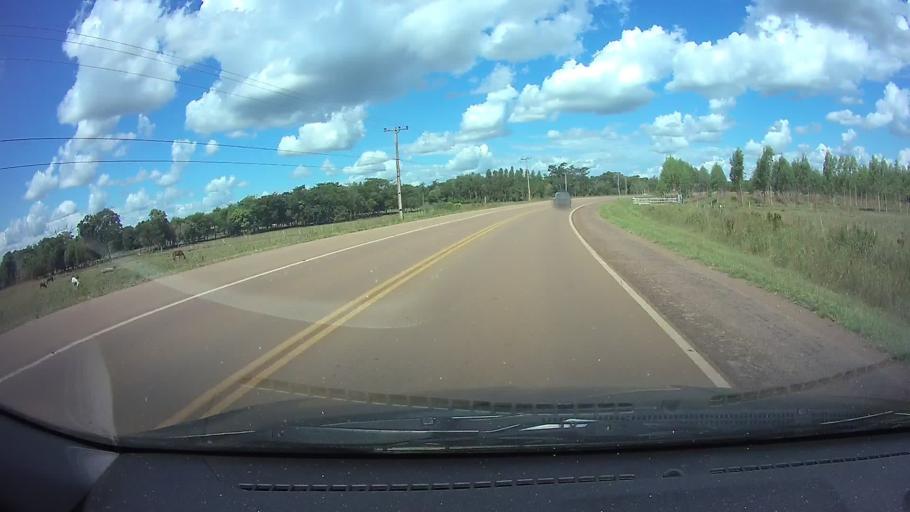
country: PY
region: Paraguari
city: La Colmena
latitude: -25.9136
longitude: -56.7119
